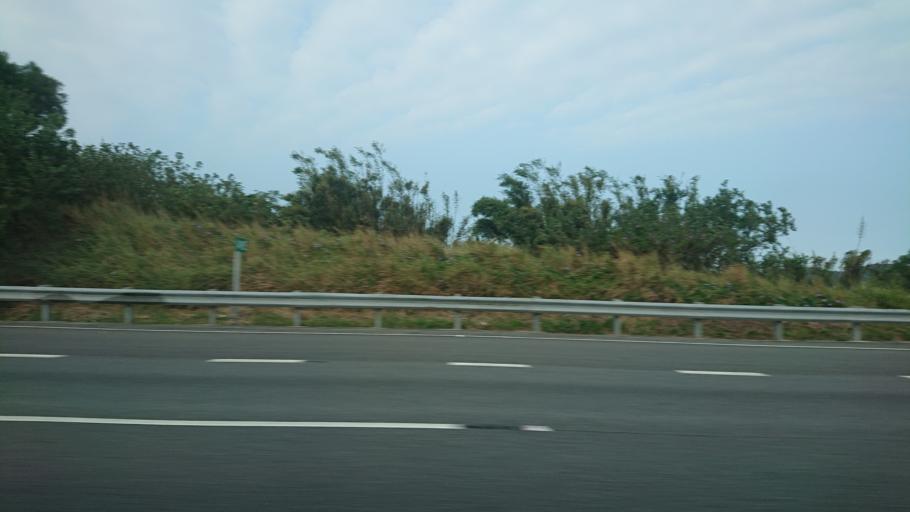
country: TW
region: Taiwan
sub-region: Miaoli
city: Miaoli
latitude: 24.4909
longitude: 120.7039
